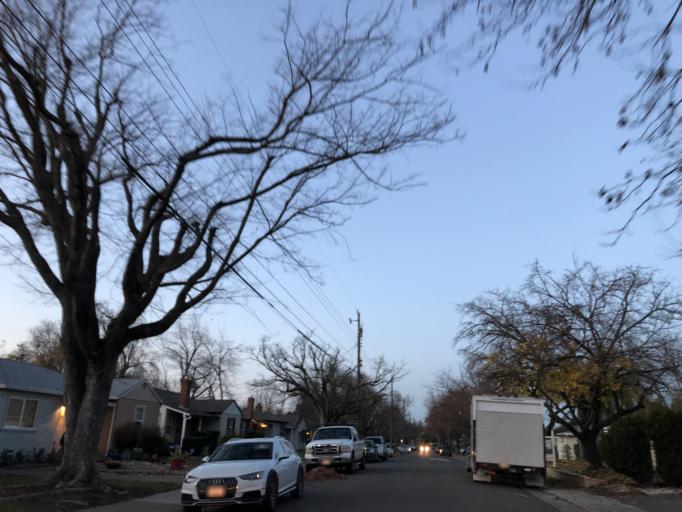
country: US
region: California
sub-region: Sacramento County
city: Parkway
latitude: 38.5505
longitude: -121.4381
